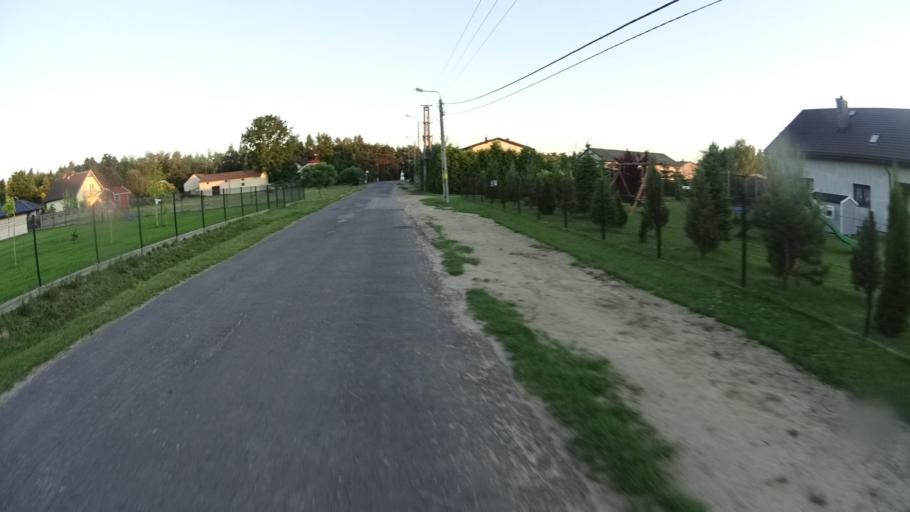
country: PL
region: Masovian Voivodeship
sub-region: Powiat warszawski zachodni
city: Jozefow
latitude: 52.2481
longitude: 20.6730
